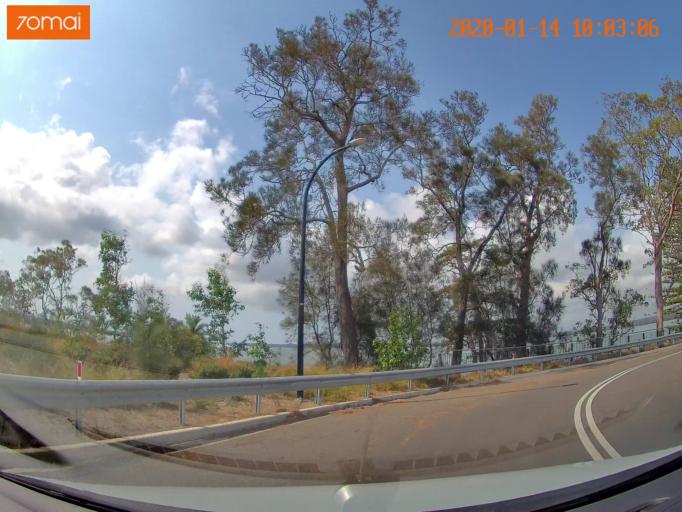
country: AU
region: New South Wales
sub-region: Wyong Shire
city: Kingfisher Shores
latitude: -33.1259
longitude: 151.5410
